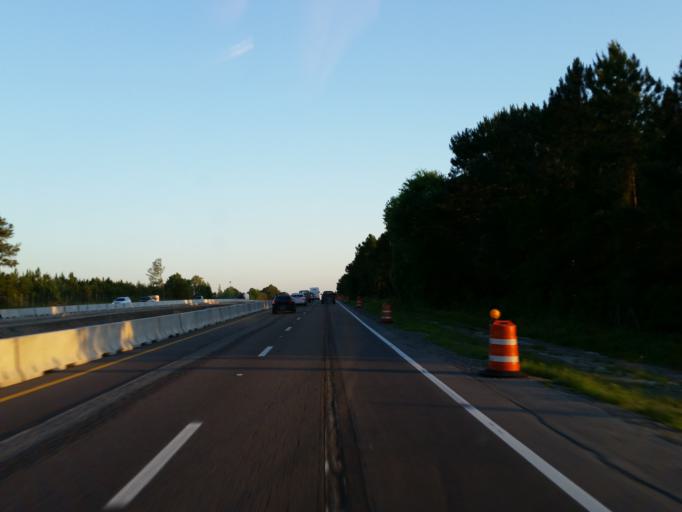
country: US
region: Florida
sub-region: Pasco County
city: San Antonio
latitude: 28.3751
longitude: -82.3197
